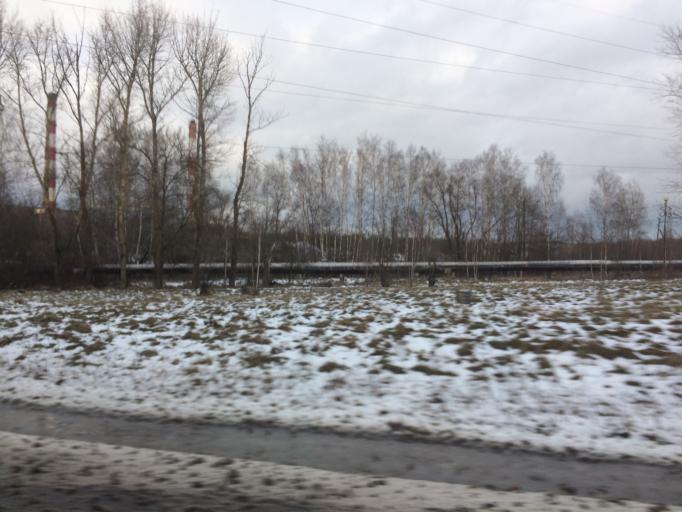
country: RU
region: Tula
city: Suvorov
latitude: 54.1302
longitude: 36.4765
